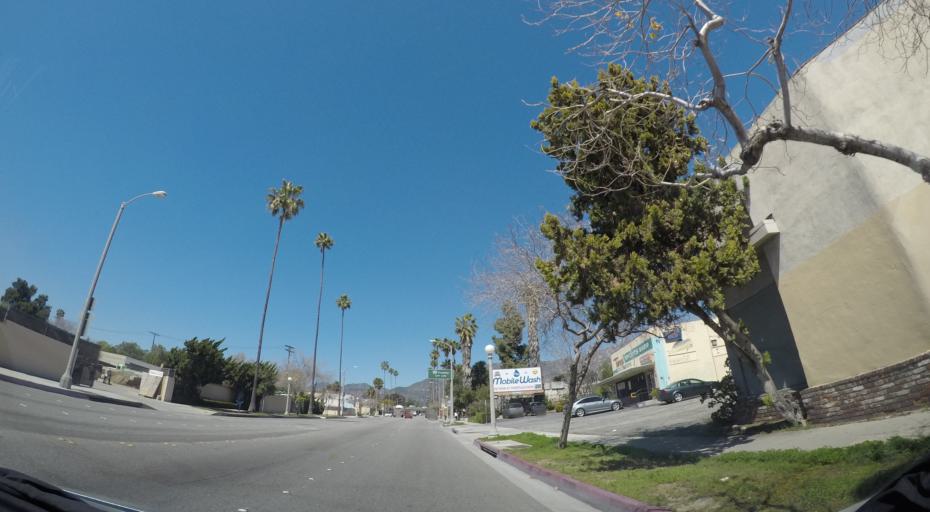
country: US
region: California
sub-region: Los Angeles County
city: Pasadena
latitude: 34.1700
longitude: -118.1595
